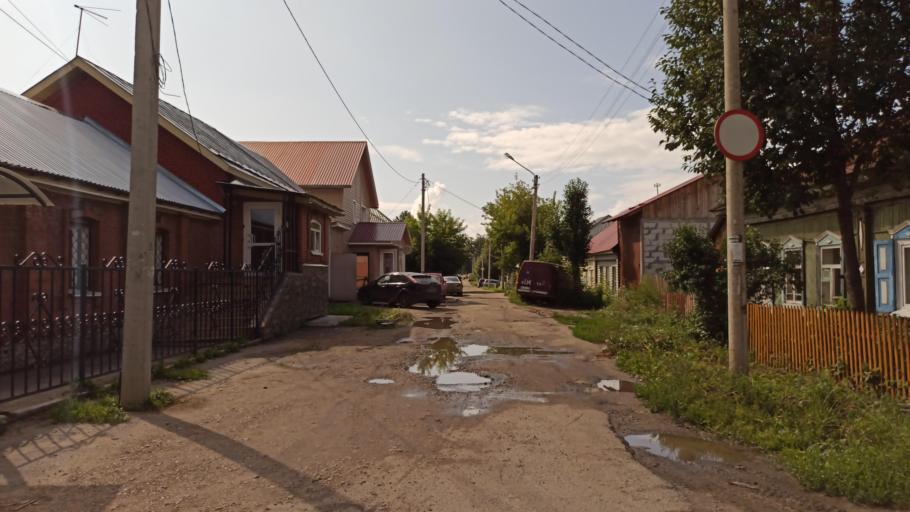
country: RU
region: Tomsk
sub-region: Tomskiy Rayon
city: Tomsk
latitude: 56.4780
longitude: 85.0081
